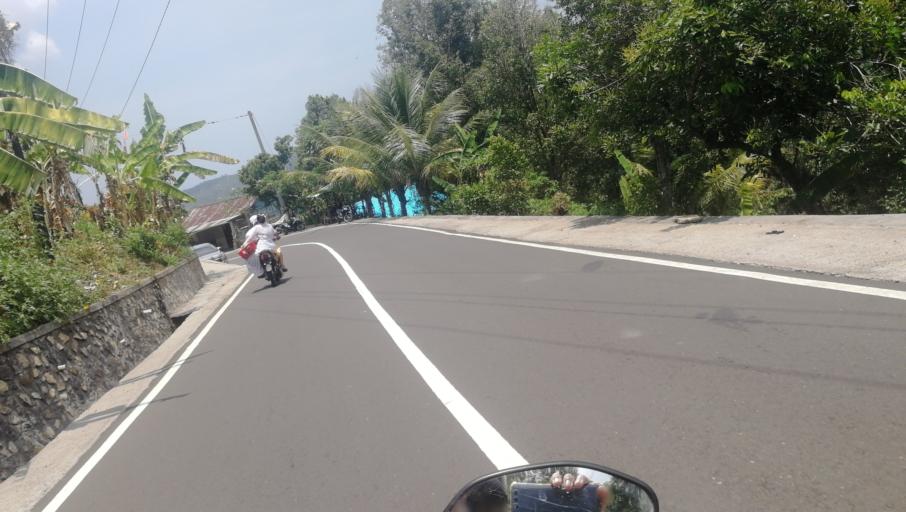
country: ID
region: Bali
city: Banjar Pedawa
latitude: -8.2636
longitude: 115.0451
